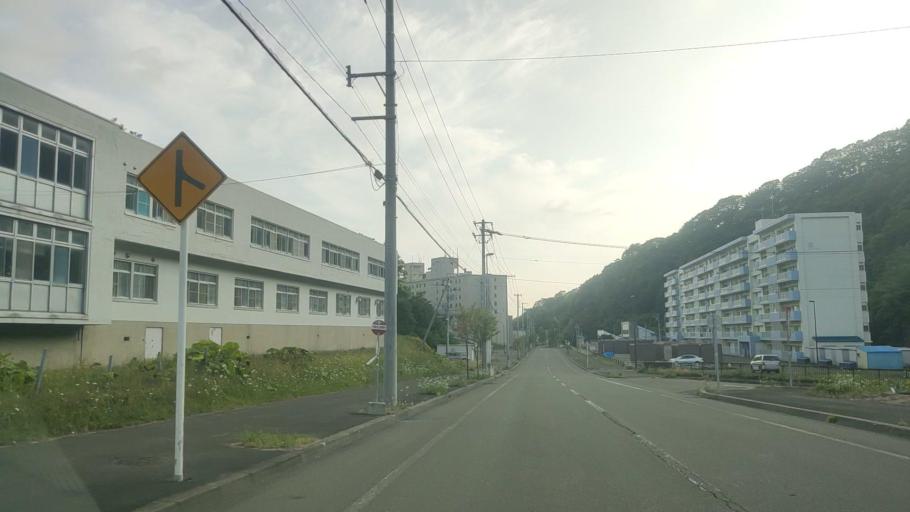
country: JP
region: Hokkaido
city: Iwamizawa
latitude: 43.0614
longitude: 141.9792
